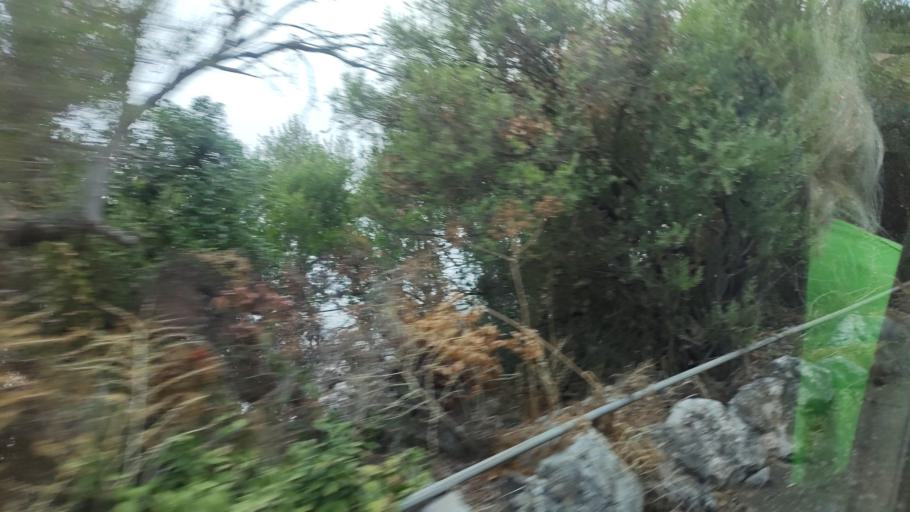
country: GI
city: Gibraltar
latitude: 36.1377
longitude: -5.3489
